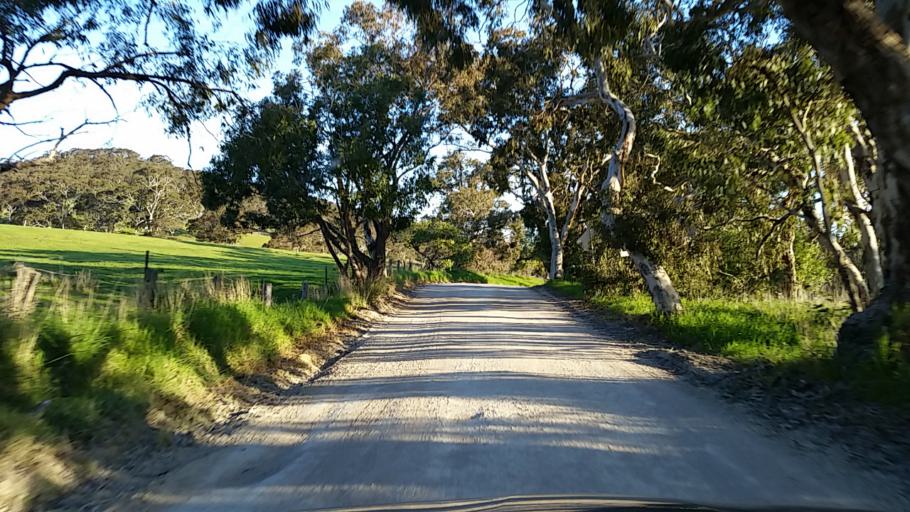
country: AU
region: South Australia
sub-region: Alexandrina
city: Mount Compass
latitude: -35.3171
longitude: 138.6706
